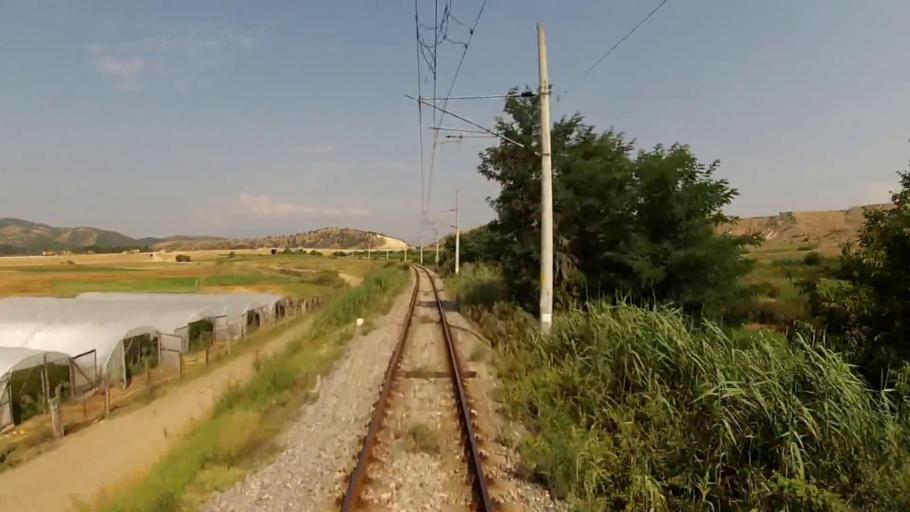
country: BG
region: Blagoevgrad
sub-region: Obshtina Petrich
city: Petrich
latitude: 41.4154
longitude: 23.3332
